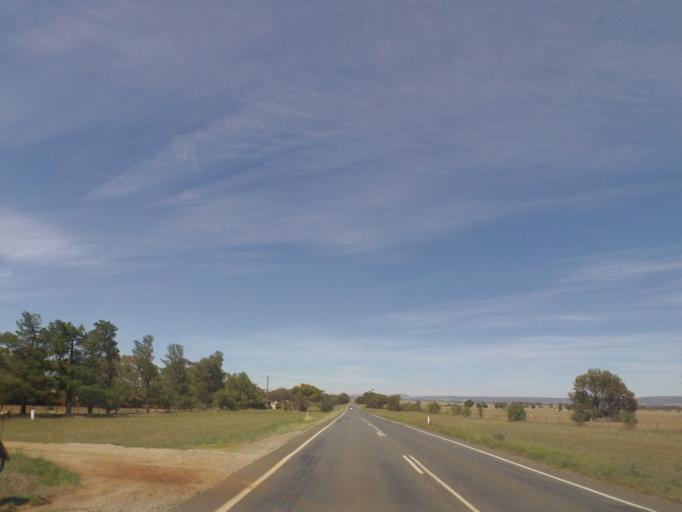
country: AU
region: Victoria
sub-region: Moorabool
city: Bacchus Marsh
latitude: -37.7893
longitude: 144.4209
